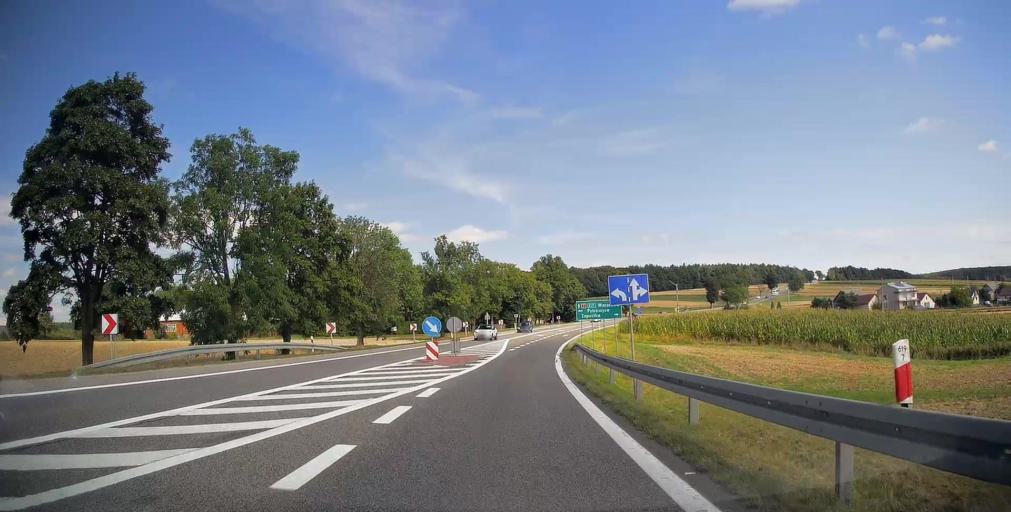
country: PL
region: Lesser Poland Voivodeship
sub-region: Powiat miechowski
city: Miechow
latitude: 50.3910
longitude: 20.0567
